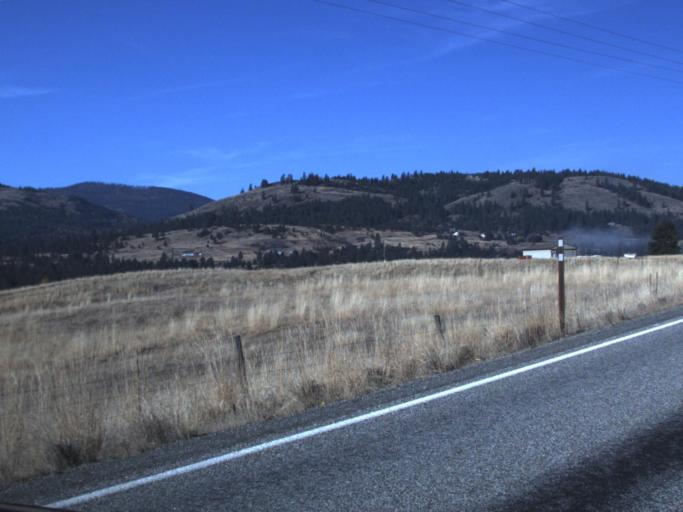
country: US
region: Washington
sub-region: Ferry County
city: Republic
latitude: 48.7344
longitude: -118.6584
